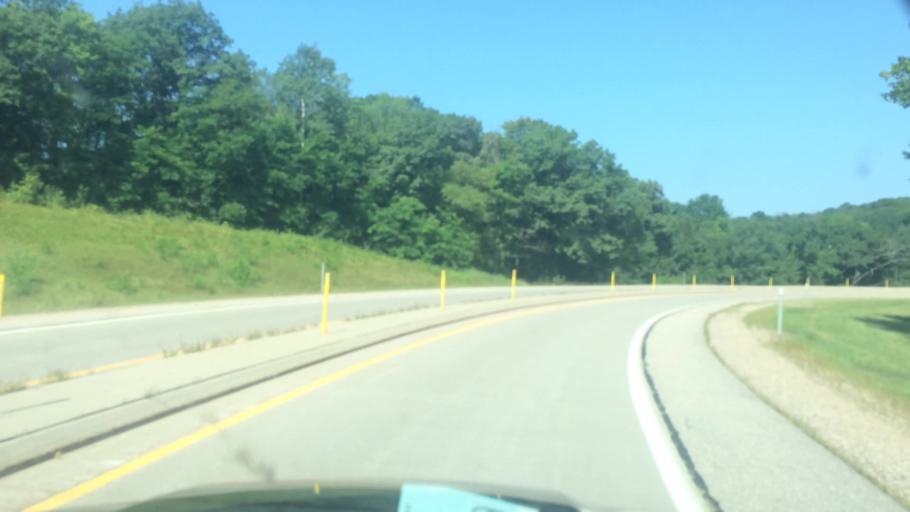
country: US
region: Wisconsin
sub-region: Waupaca County
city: Waupaca
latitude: 44.3363
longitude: -89.0688
